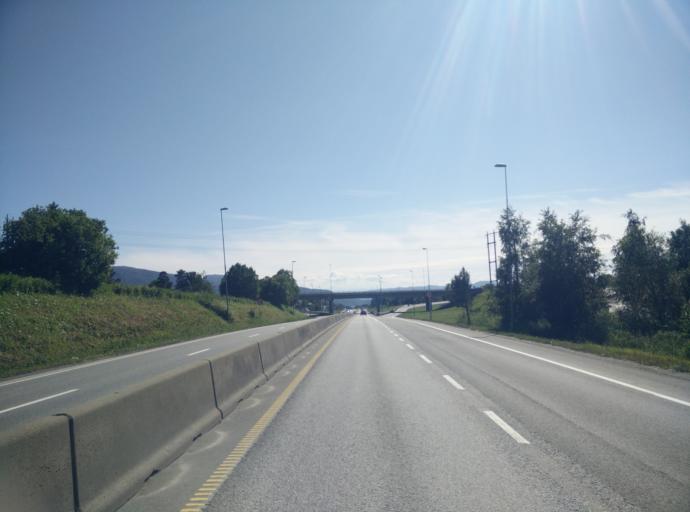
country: NO
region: Sor-Trondelag
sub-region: Melhus
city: Melhus
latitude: 63.3353
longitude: 10.3584
